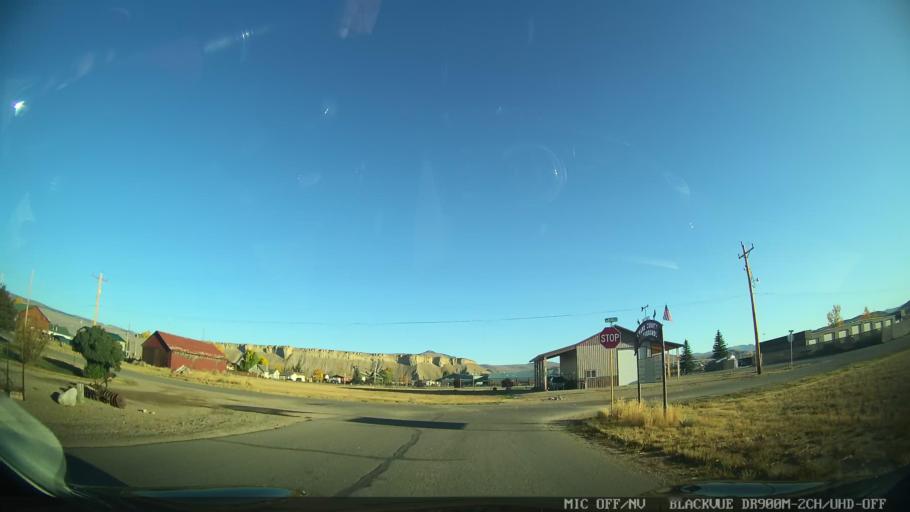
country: US
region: Colorado
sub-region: Grand County
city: Kremmling
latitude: 40.0571
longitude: -106.3805
